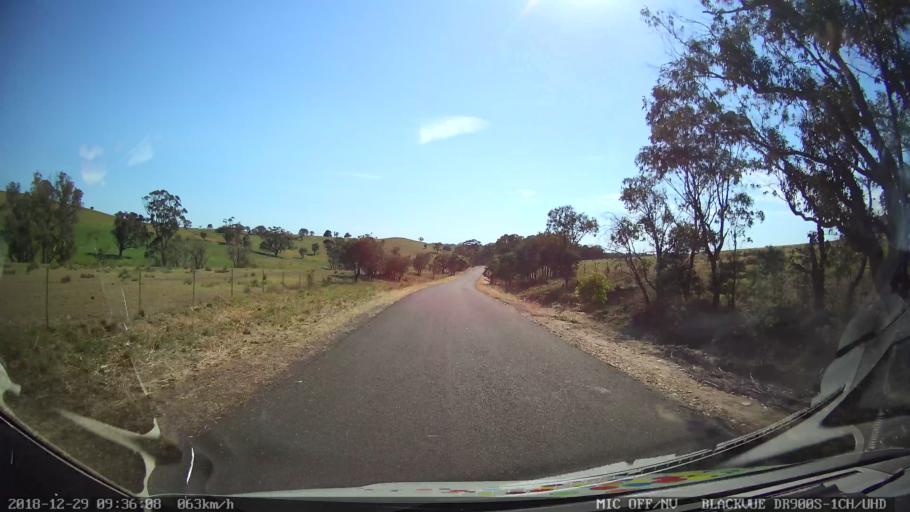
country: AU
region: New South Wales
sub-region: Upper Lachlan Shire
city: Crookwell
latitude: -34.6339
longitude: 149.3603
